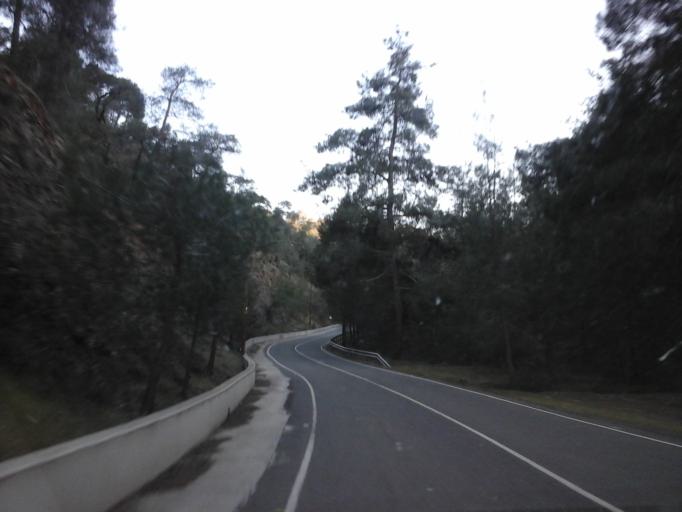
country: CY
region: Lefkosia
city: Kakopetria
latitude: 35.0536
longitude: 32.9819
